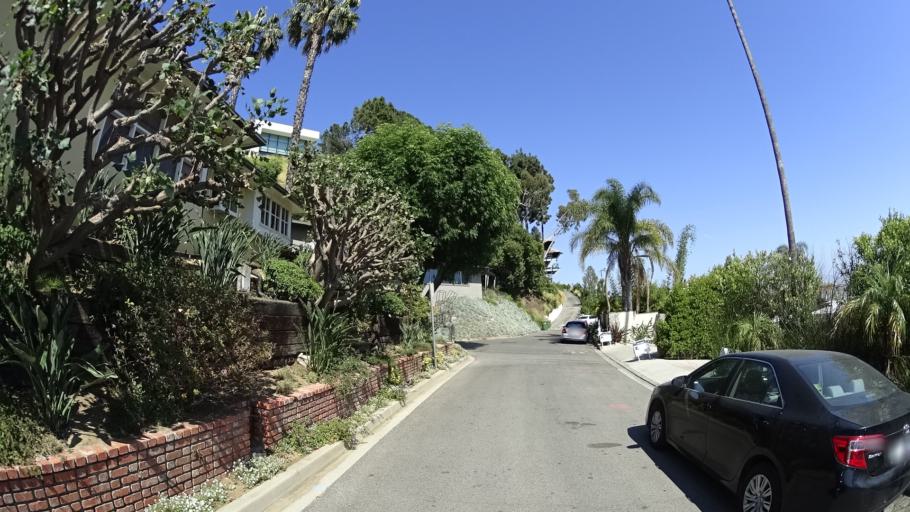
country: US
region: California
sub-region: Los Angeles County
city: West Hollywood
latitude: 34.0955
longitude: -118.3796
